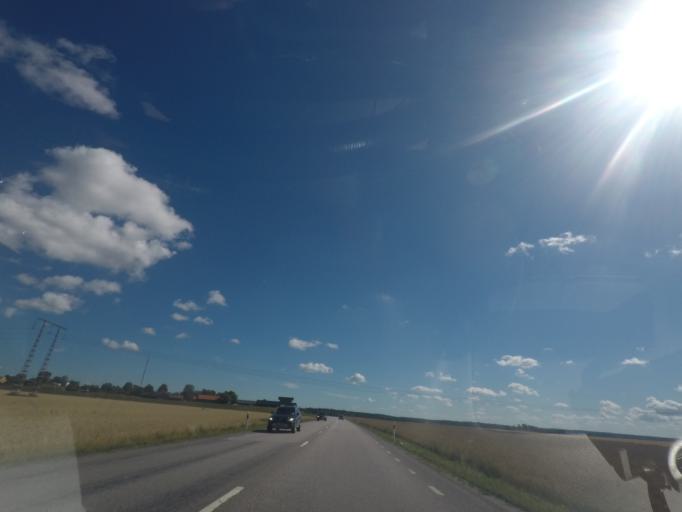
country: SE
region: Uppsala
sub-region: Uppsala Kommun
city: Saevja
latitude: 59.8445
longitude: 17.7446
